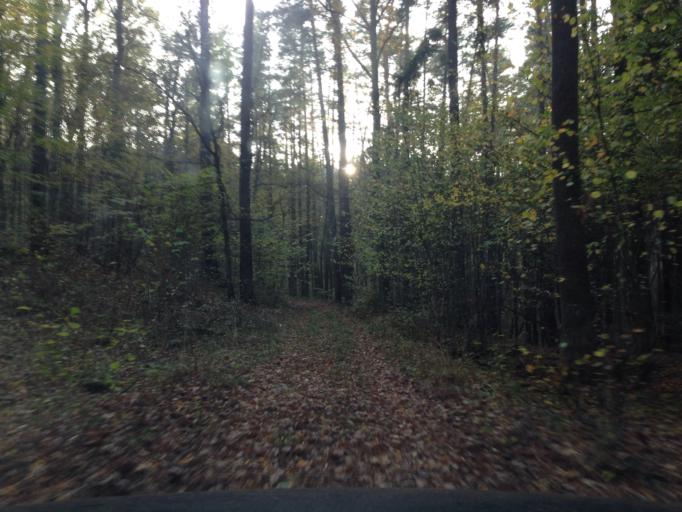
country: PL
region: Kujawsko-Pomorskie
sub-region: Powiat brodnicki
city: Gorzno
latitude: 53.2587
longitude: 19.7127
